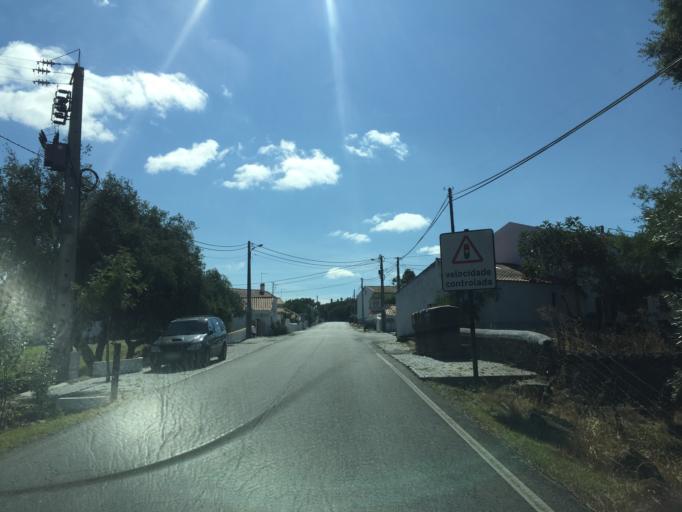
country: PT
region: Portalegre
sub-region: Marvao
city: Marvao
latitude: 39.4352
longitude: -7.3641
